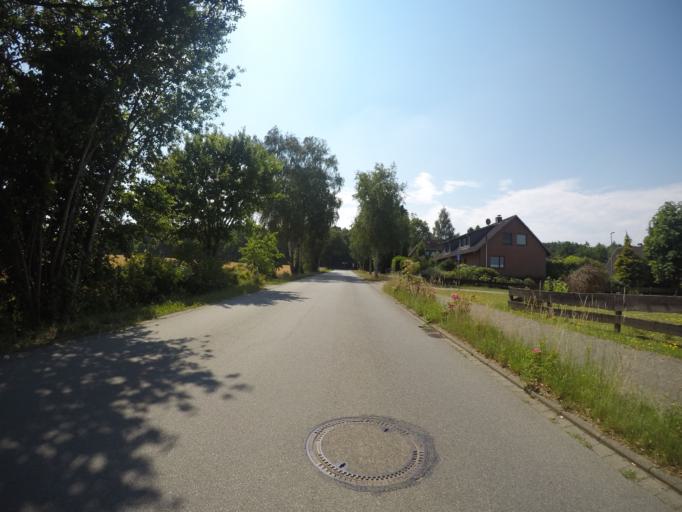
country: DE
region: Lower Saxony
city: Buchholz in der Nordheide
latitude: 53.3107
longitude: 9.8221
